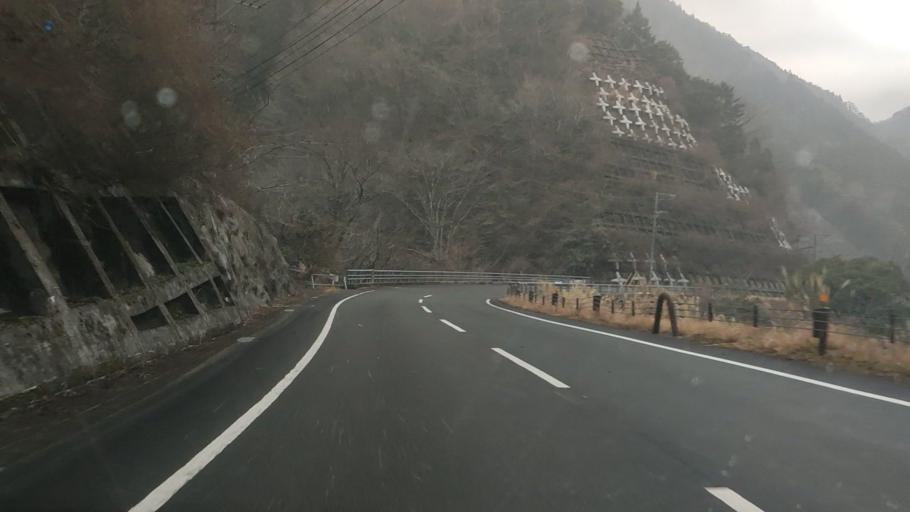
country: JP
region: Kumamoto
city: Matsubase
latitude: 32.5494
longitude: 130.9355
